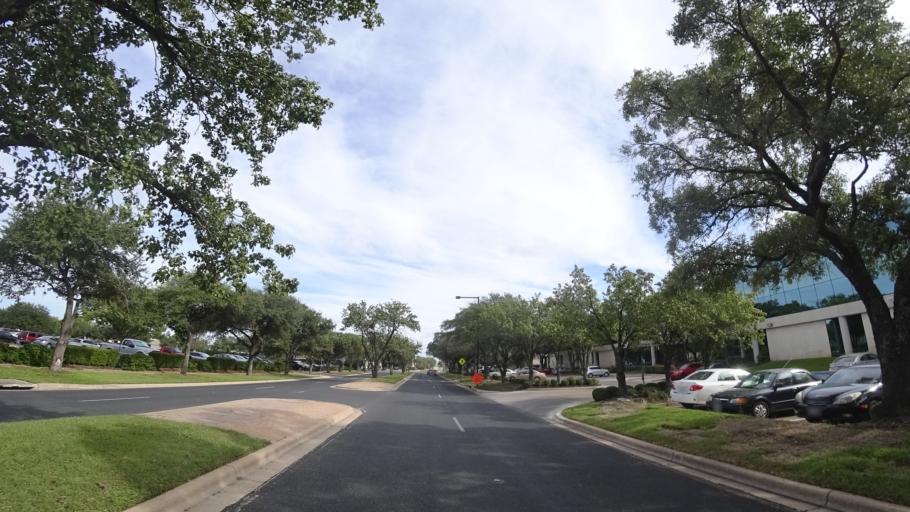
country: US
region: Texas
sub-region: Travis County
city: Austin
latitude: 30.2129
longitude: -97.7496
